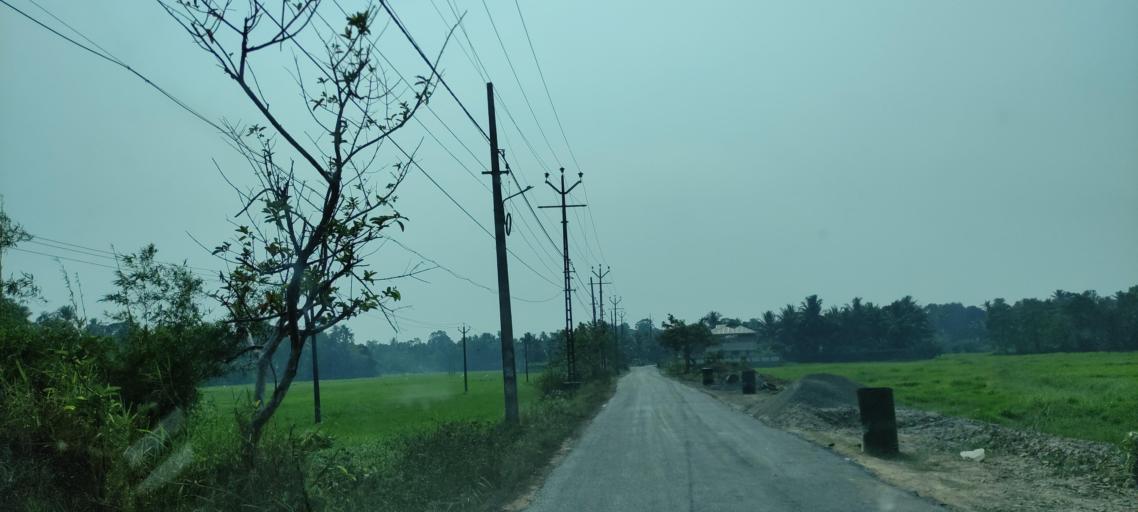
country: IN
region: Kerala
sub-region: Pattanamtitta
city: Tiruvalla
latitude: 9.3608
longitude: 76.4995
